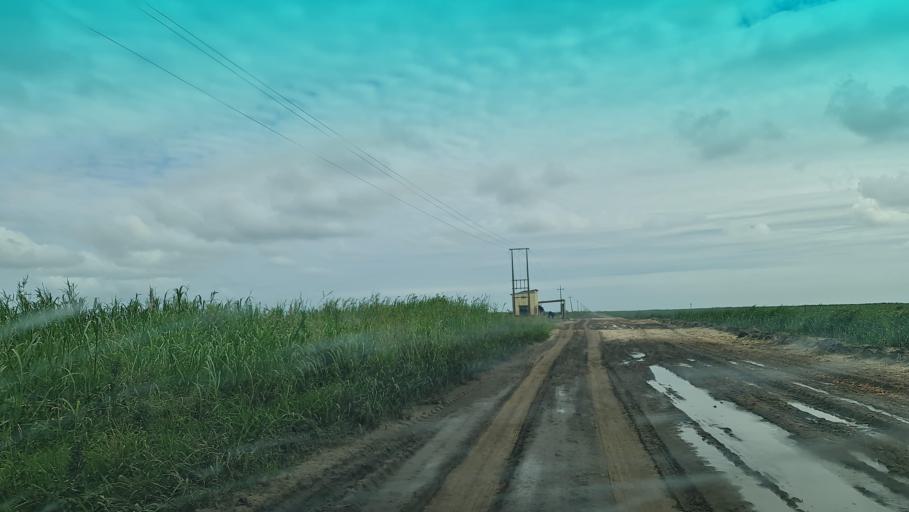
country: MZ
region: Maputo
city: Manhica
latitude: -25.4446
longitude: 32.8399
